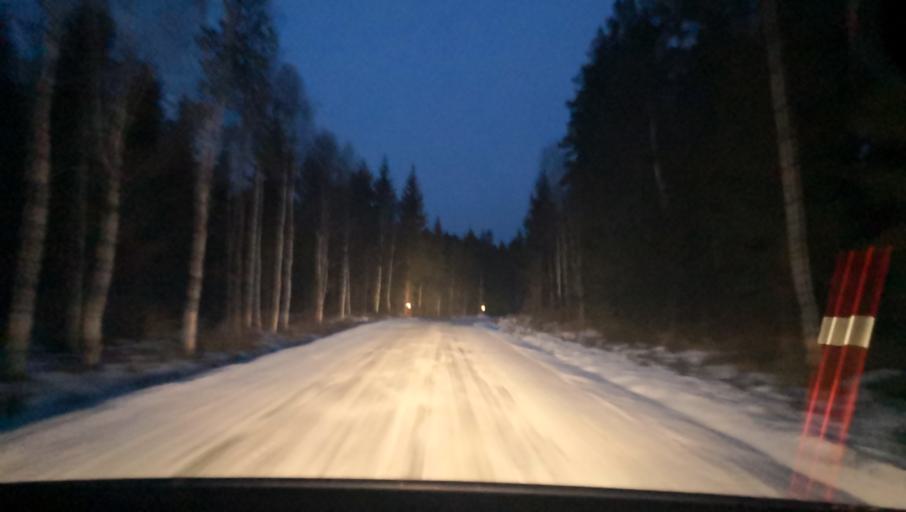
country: SE
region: Uppsala
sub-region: Heby Kommun
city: Tarnsjo
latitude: 60.2516
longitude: 16.7333
